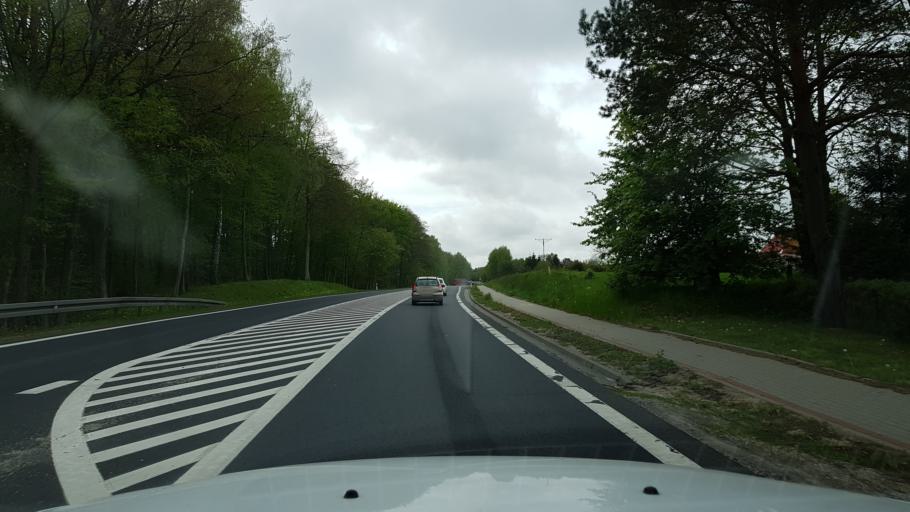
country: PL
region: West Pomeranian Voivodeship
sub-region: Powiat slawienski
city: Darlowo
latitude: 54.2773
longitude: 16.4738
